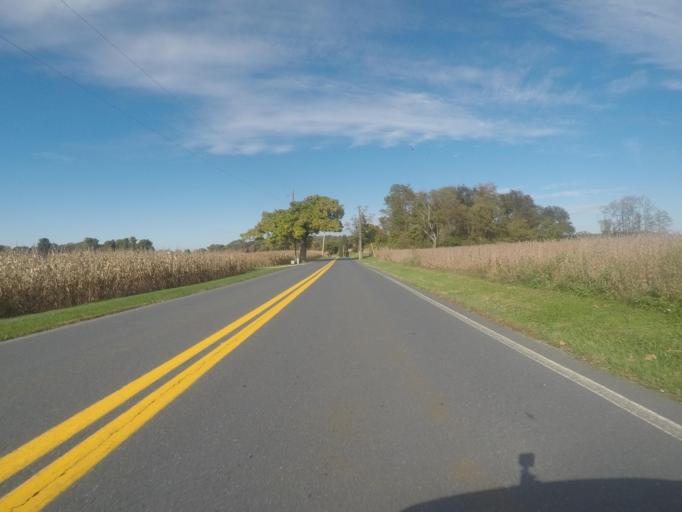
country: US
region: Maryland
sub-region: Carroll County
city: Hampstead
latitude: 39.5394
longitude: -76.8645
